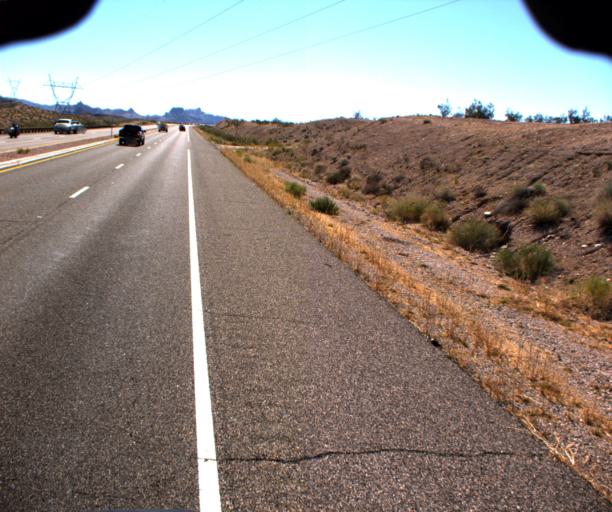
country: US
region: Nevada
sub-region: Clark County
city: Laughlin
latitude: 35.1898
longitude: -114.5135
